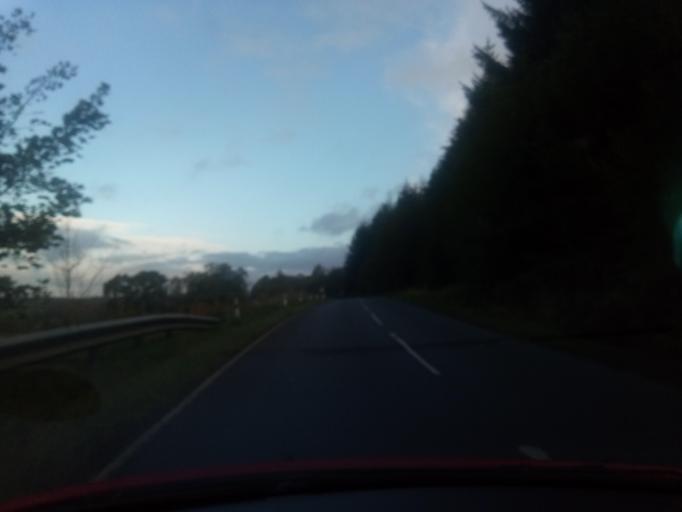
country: GB
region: Scotland
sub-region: The Scottish Borders
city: Hawick
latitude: 55.3625
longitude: -2.6504
